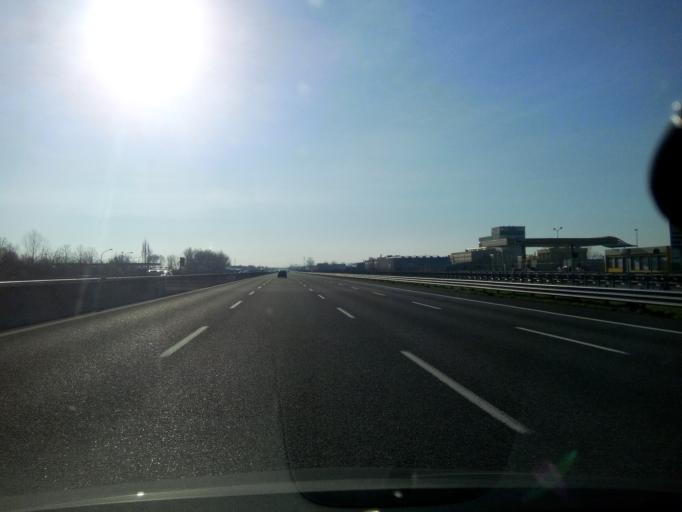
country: IT
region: Emilia-Romagna
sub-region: Provincia di Modena
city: Montale
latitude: 44.6083
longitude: 10.9084
